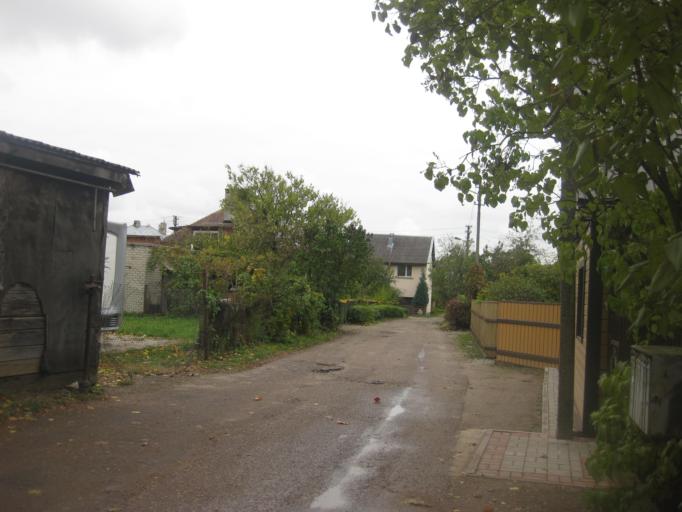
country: LT
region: Kauno apskritis
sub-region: Kaunas
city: Kaunas
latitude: 54.9076
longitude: 23.9091
